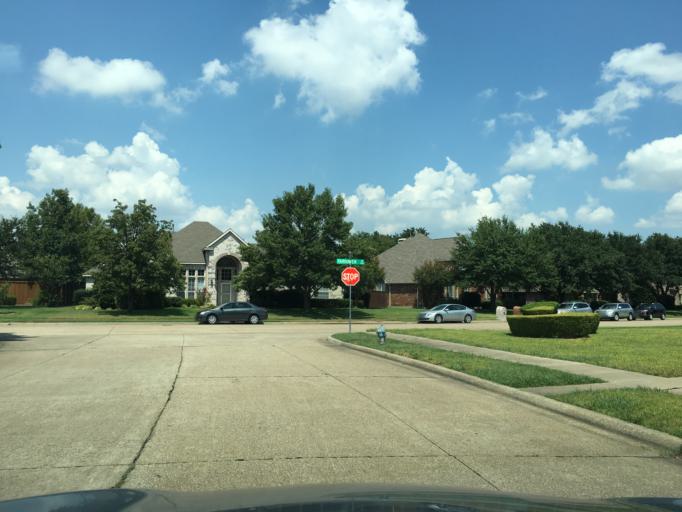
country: US
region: Texas
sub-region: Dallas County
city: Garland
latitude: 32.9405
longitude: -96.6440
